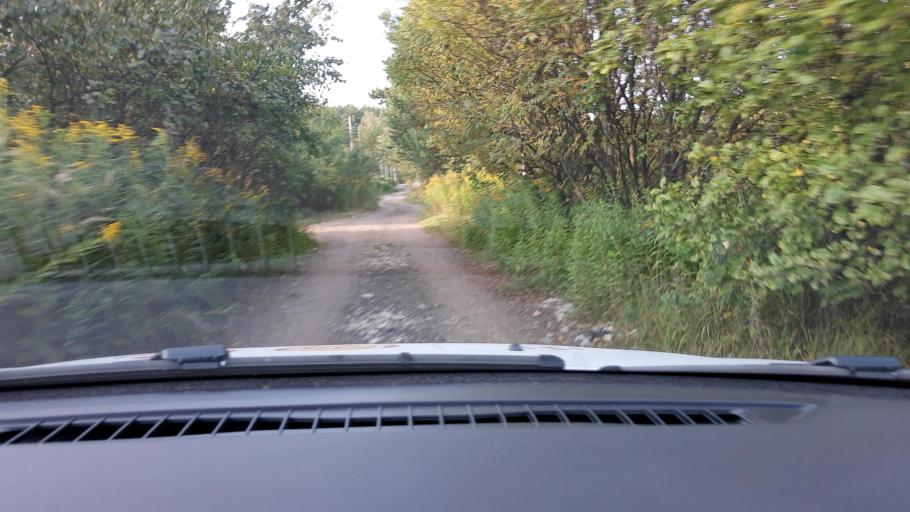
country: RU
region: Nizjnij Novgorod
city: Sitniki
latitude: 56.4204
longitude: 44.0696
